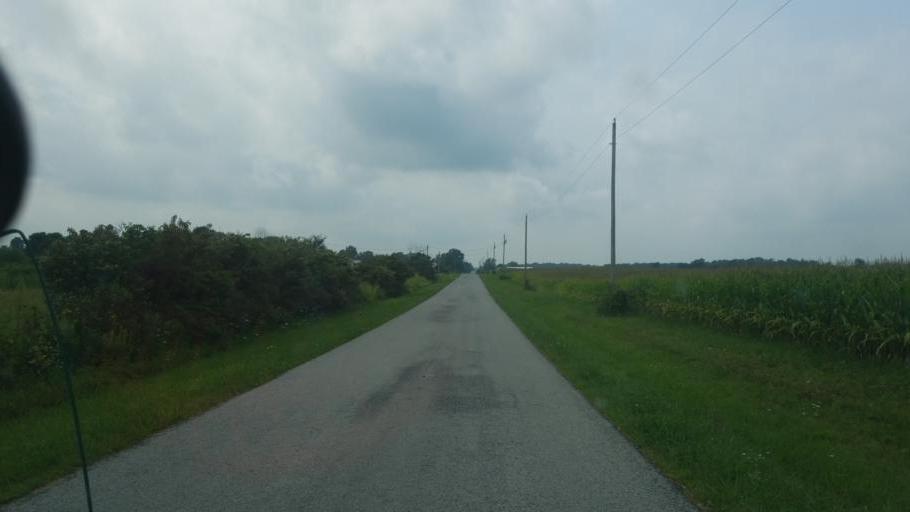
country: US
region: Ohio
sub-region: Huron County
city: Greenwich
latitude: 41.0616
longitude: -82.4633
